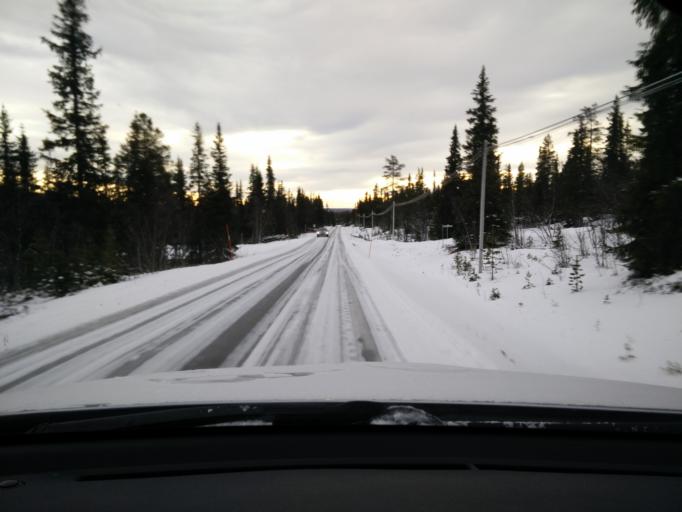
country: SE
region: Jaemtland
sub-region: Bergs Kommun
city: Hoverberg
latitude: 62.4875
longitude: 14.1190
